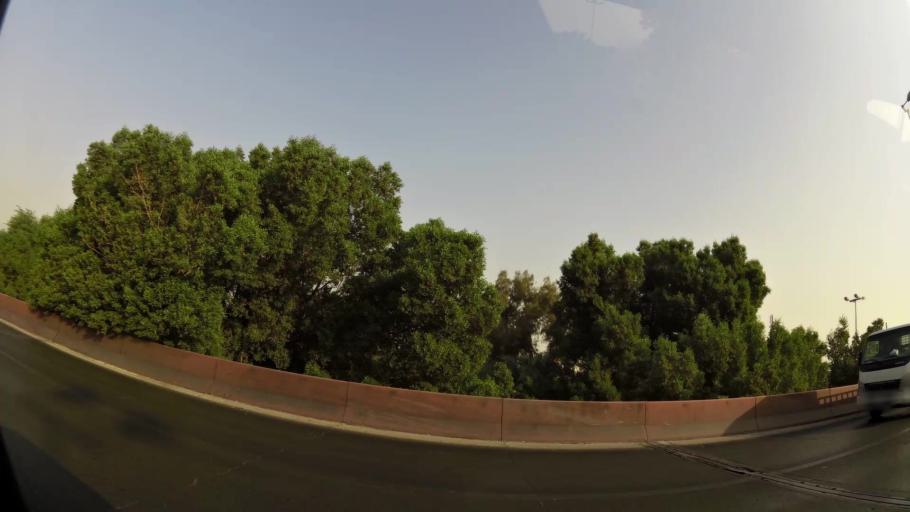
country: KW
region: Muhafazat Hawalli
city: Hawalli
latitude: 29.3206
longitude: 47.9927
